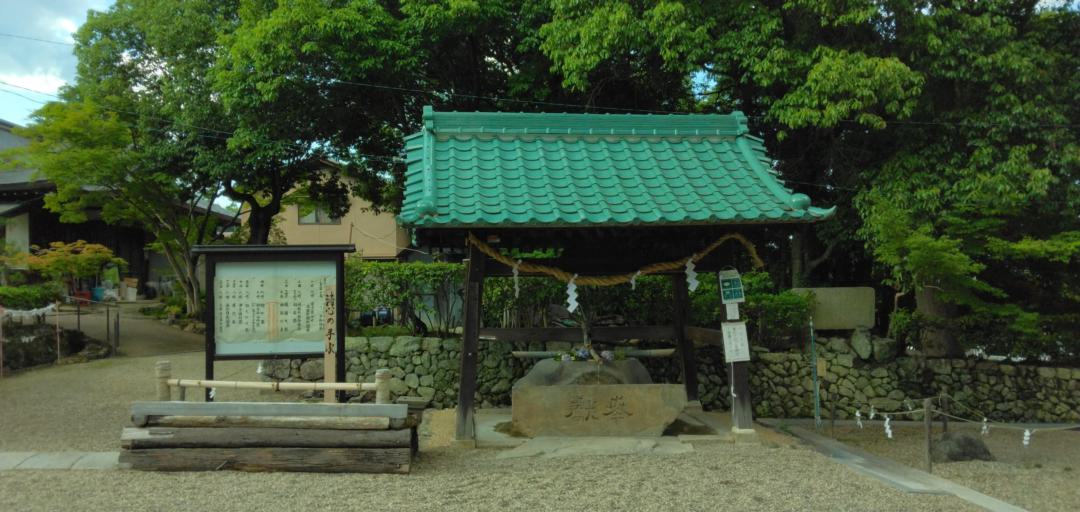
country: JP
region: Osaka
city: Kashihara
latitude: 34.5930
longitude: 135.6883
